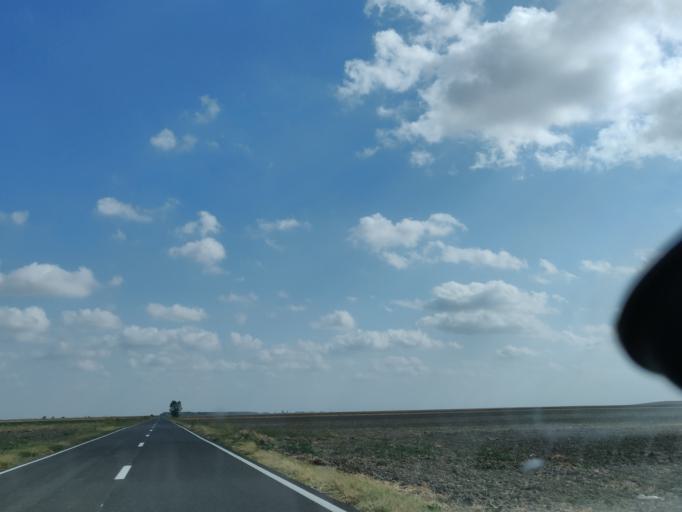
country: RO
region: Vrancea
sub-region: Comuna Ciorasti
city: Mihalceni
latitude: 45.4410
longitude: 27.3352
